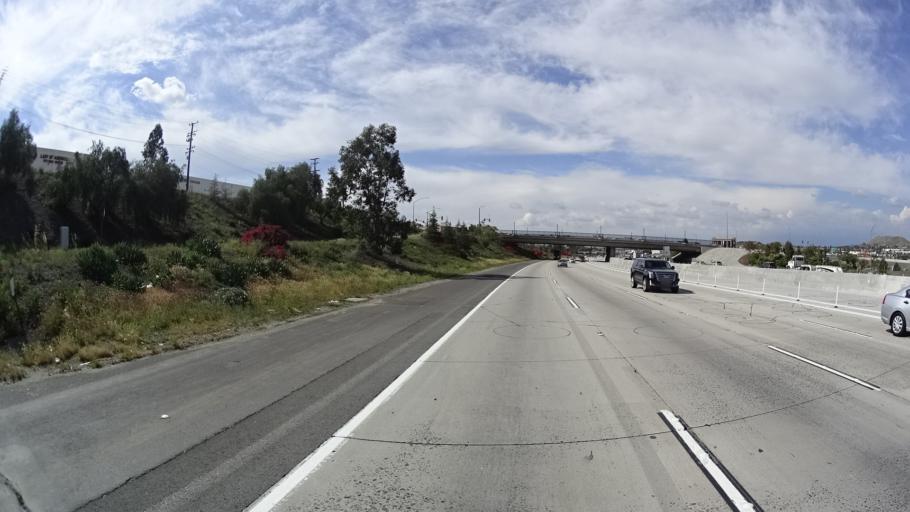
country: US
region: California
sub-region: Riverside County
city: Home Gardens
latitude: 33.8646
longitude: -117.5414
